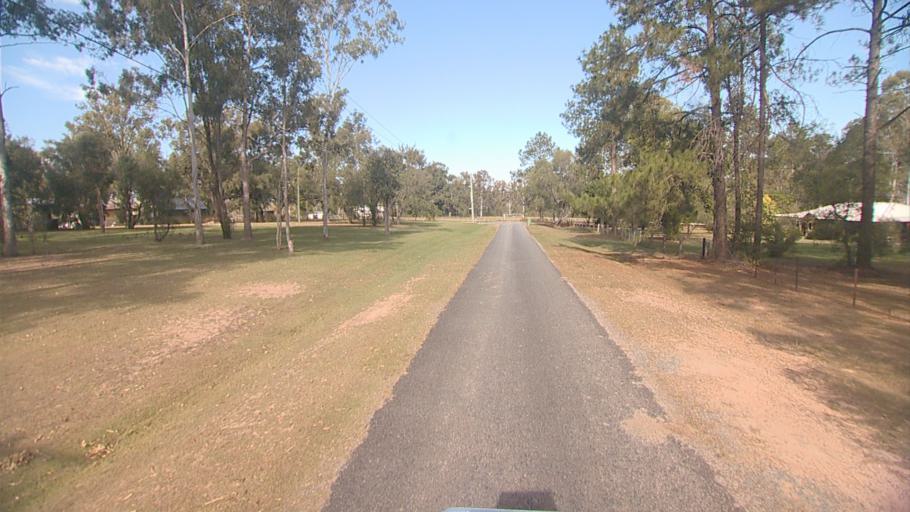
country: AU
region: Queensland
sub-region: Logan
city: North Maclean
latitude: -27.7830
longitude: 152.9932
